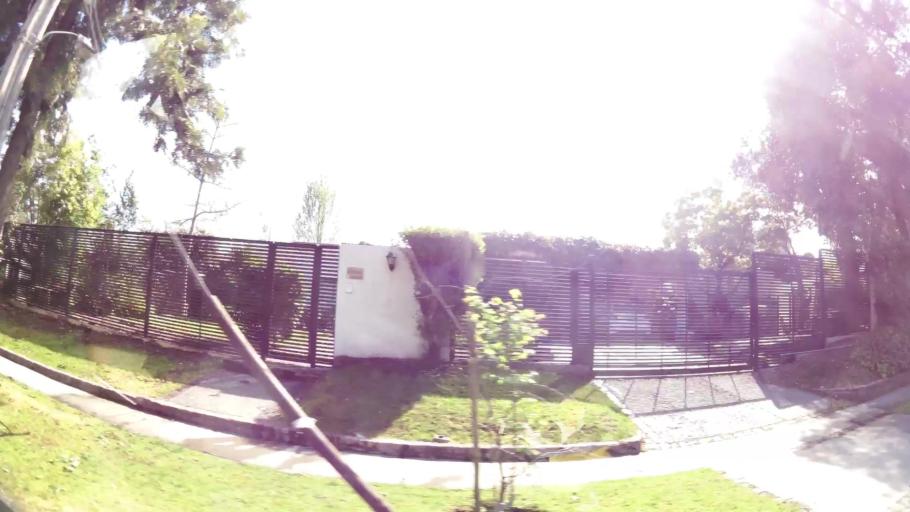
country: CL
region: Santiago Metropolitan
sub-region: Provincia de Santiago
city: Villa Presidente Frei, Nunoa, Santiago, Chile
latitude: -33.4386
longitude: -70.5420
